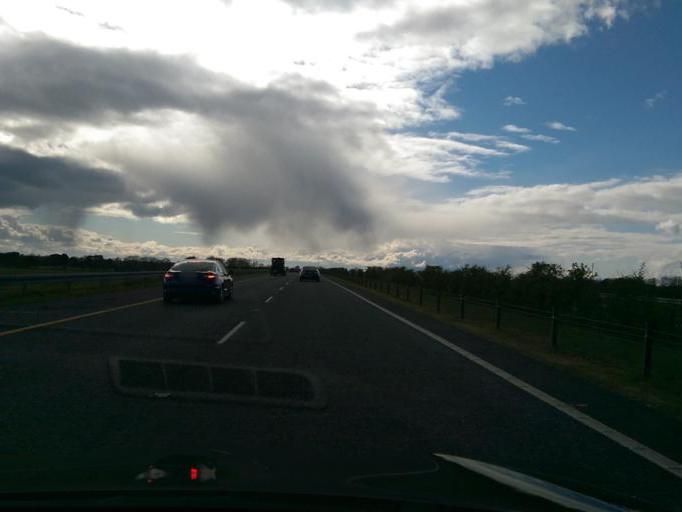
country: IE
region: Leinster
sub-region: An Mhi
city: Enfield
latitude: 53.4044
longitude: -6.8083
